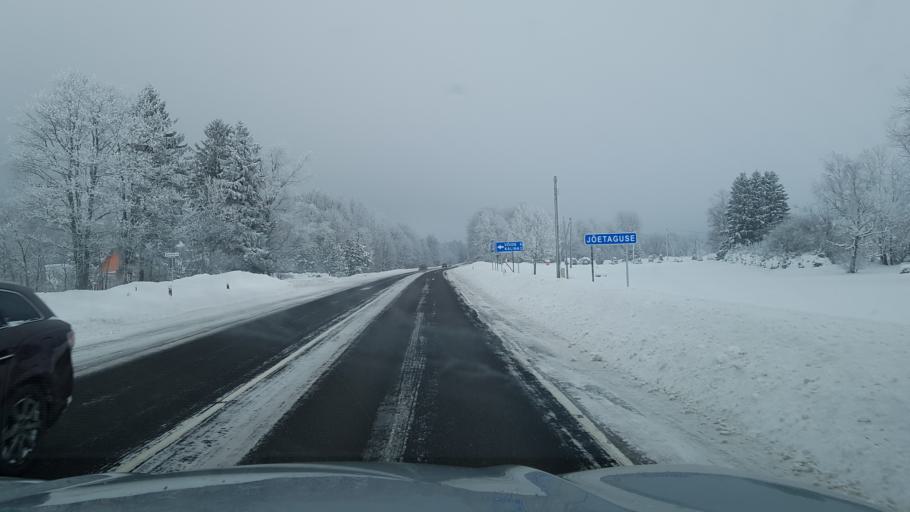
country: EE
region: Ida-Virumaa
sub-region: Johvi vald
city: Johvi
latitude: 59.2714
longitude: 27.3858
